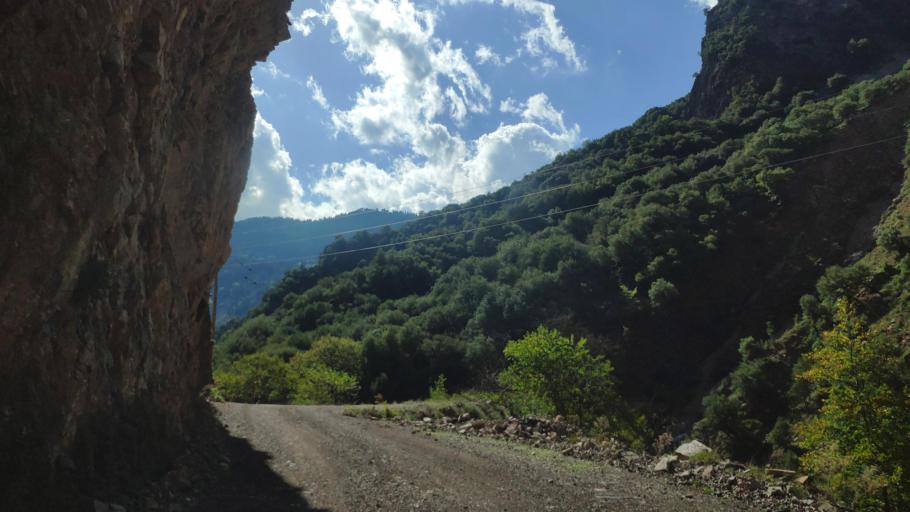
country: GR
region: Central Greece
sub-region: Nomos Evrytanias
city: Kerasochori
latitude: 39.1357
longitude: 21.6367
